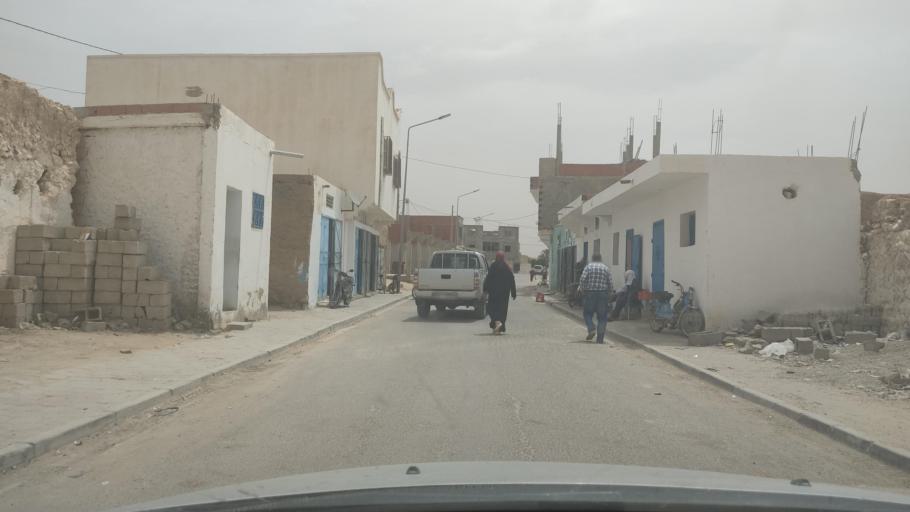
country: TN
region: Gafsa
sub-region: Gafsa Municipality
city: Gafsa
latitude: 34.3343
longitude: 8.9528
